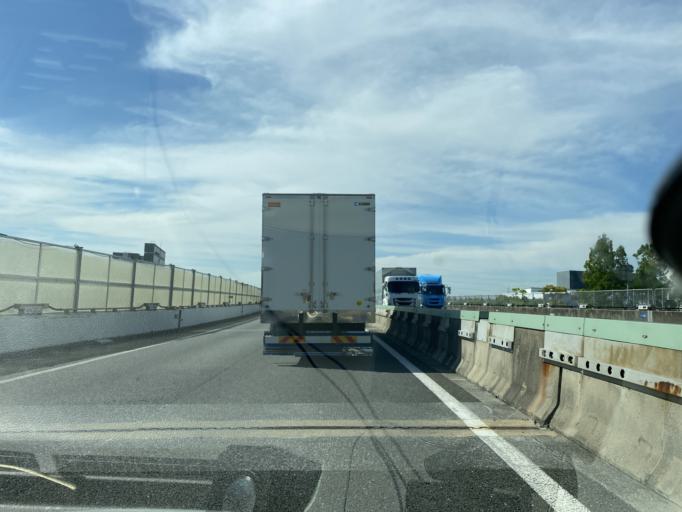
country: JP
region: Osaka
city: Ibaraki
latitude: 34.7767
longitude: 135.5610
